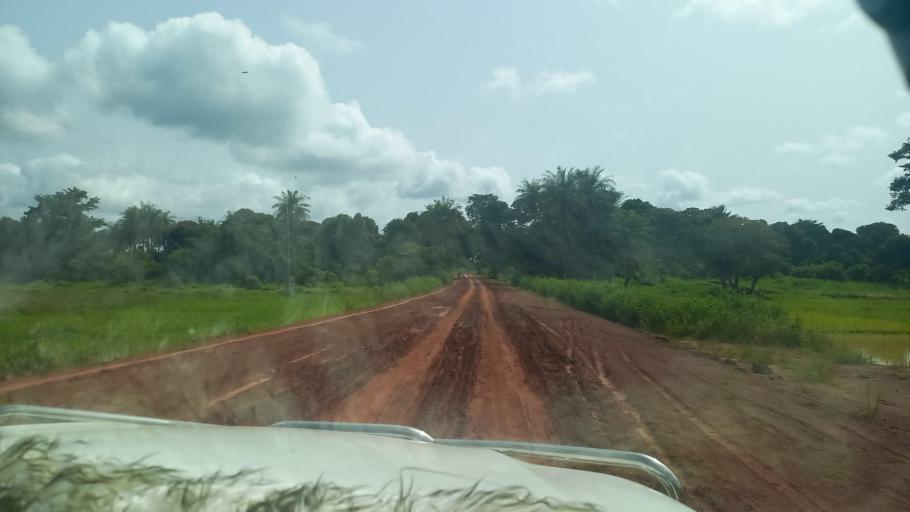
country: SN
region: Ziguinchor
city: Bignona
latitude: 12.7553
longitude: -16.2724
